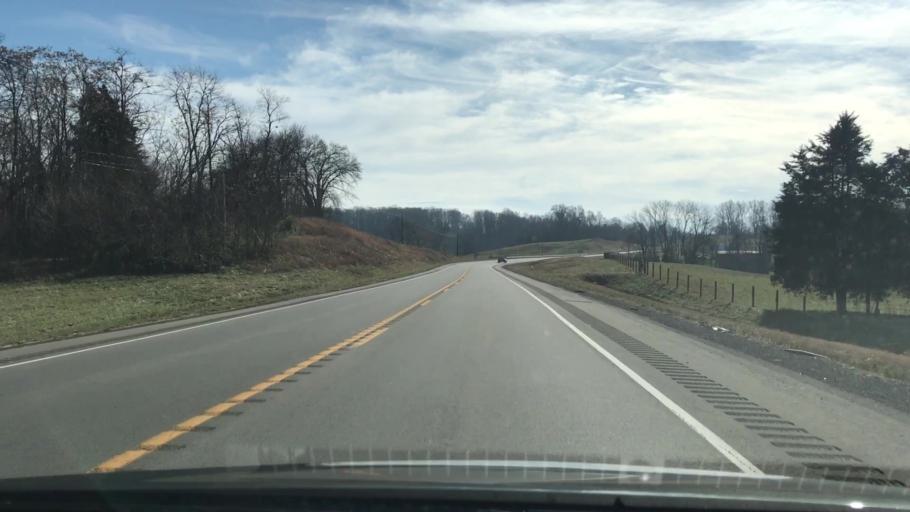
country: US
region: Kentucky
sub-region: Monroe County
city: Tompkinsville
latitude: 36.7813
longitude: -85.6853
